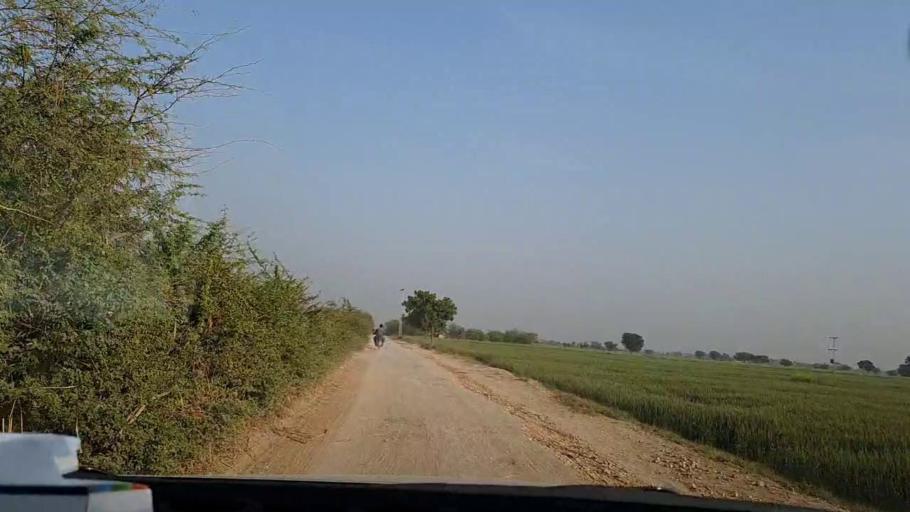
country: PK
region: Sindh
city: Tando Ghulam Ali
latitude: 25.2126
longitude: 68.8878
